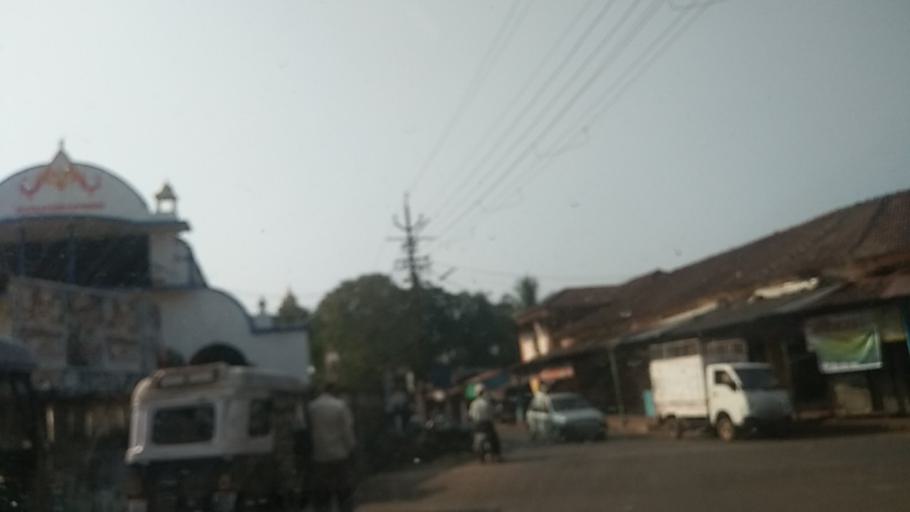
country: IN
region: Goa
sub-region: North Goa
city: Pernem
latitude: 15.7175
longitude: 73.7974
